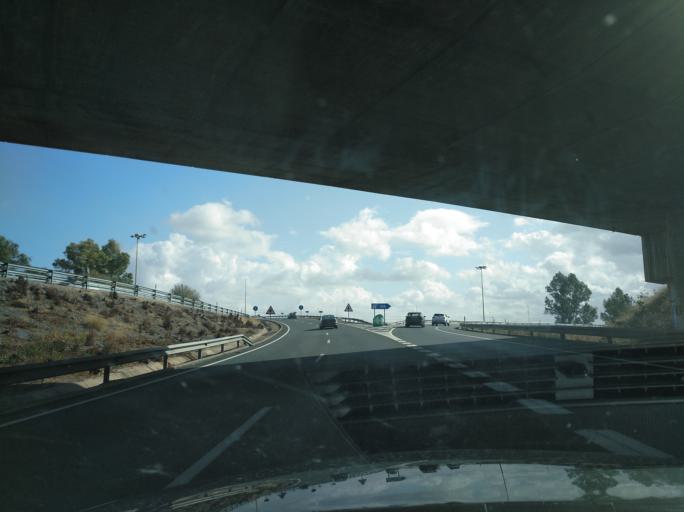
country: ES
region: Andalusia
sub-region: Provincia de Sevilla
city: Camas
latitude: 37.3883
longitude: -6.0276
